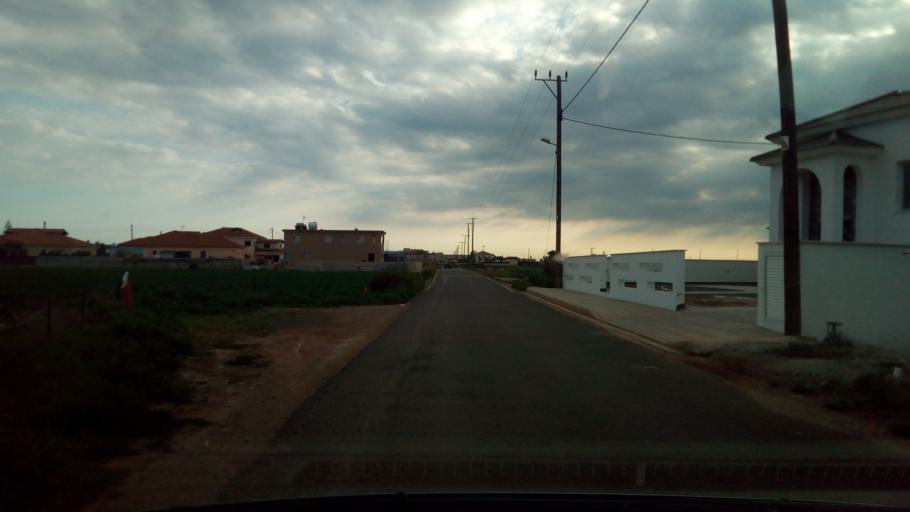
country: CY
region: Ammochostos
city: Avgorou
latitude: 34.9818
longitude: 33.8434
